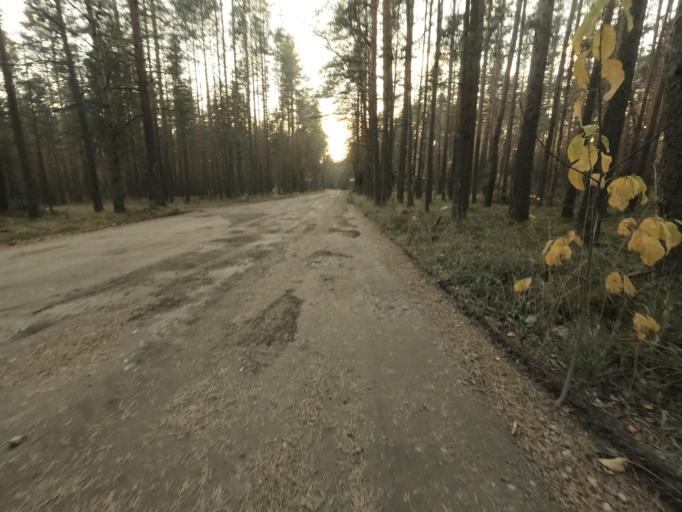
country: RU
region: St.-Petersburg
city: Repino
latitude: 60.1914
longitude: 29.8888
